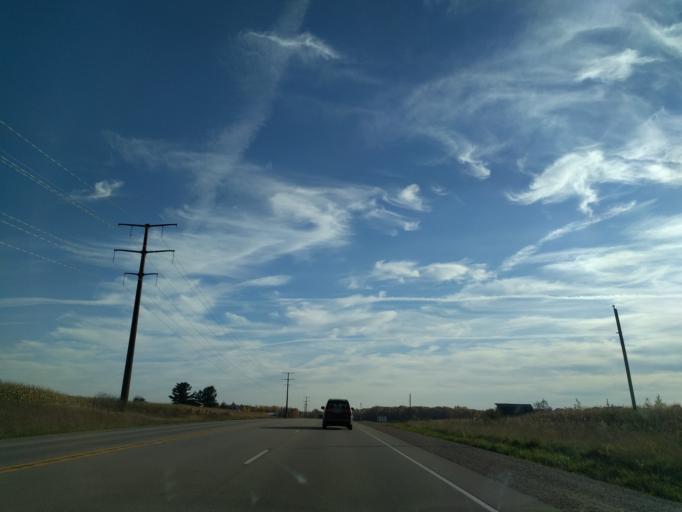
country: US
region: Wisconsin
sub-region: Marinette County
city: Peshtigo
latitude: 45.2703
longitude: -87.9907
